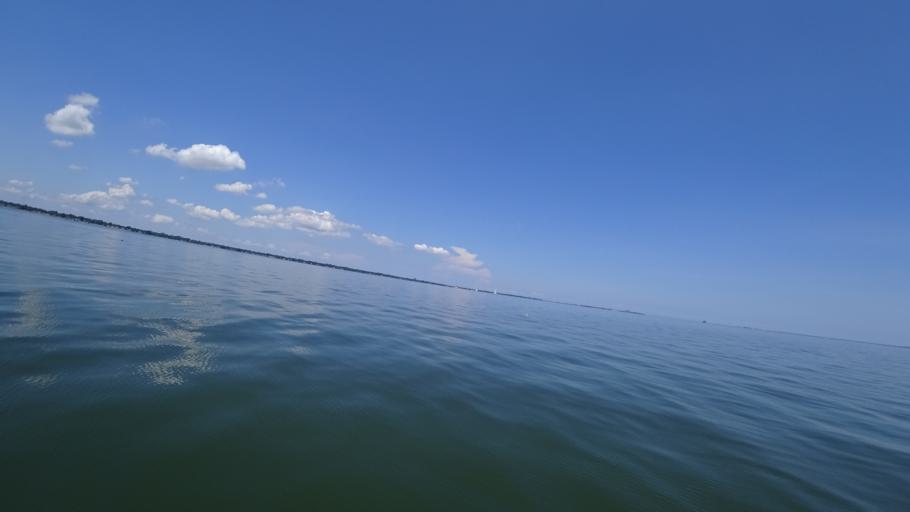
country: US
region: Virginia
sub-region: City of Newport News
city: Newport News
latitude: 36.9704
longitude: -76.3733
